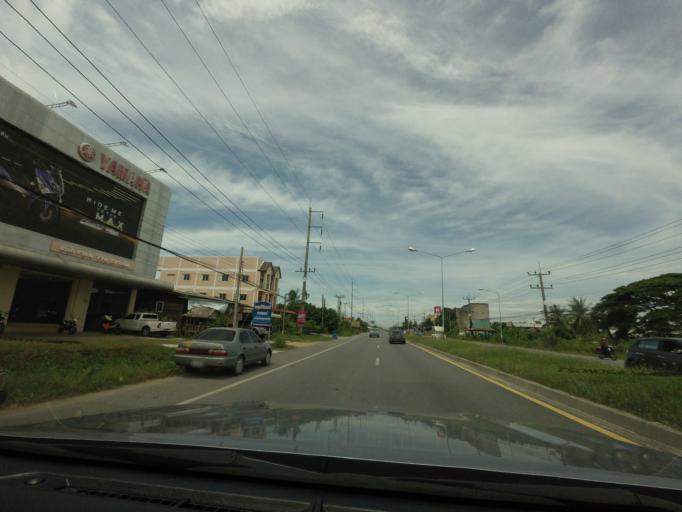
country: TH
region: Songkhla
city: Ranot
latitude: 7.7733
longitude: 100.3559
